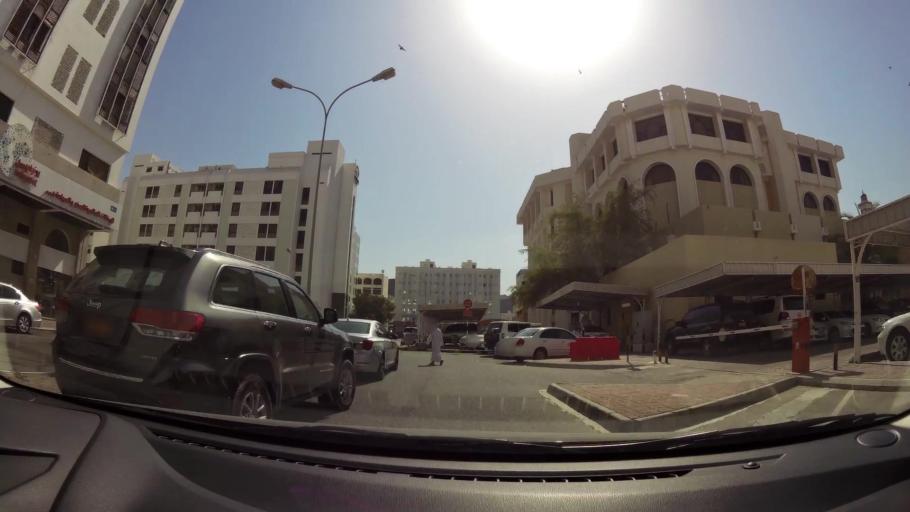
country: OM
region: Muhafazat Masqat
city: Muscat
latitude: 23.5968
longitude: 58.5485
